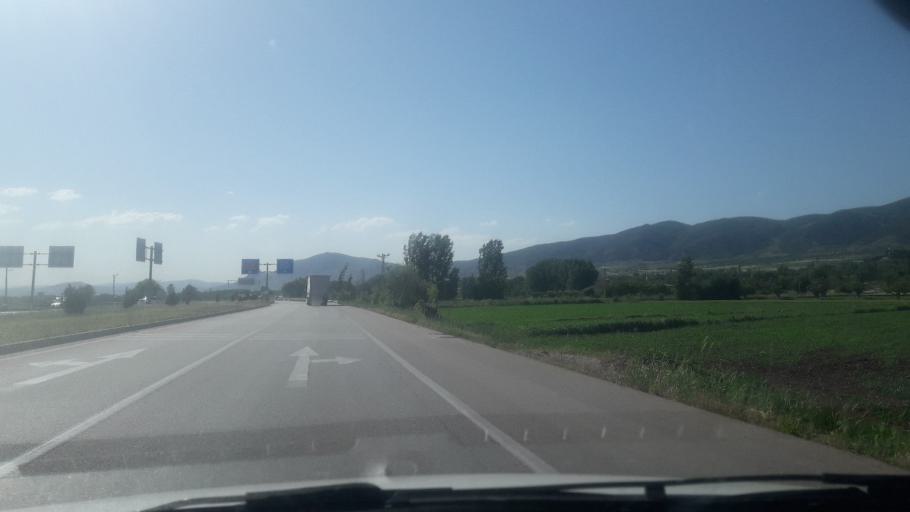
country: TR
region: Tokat
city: Dokmetepe
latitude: 40.3068
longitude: 36.3016
